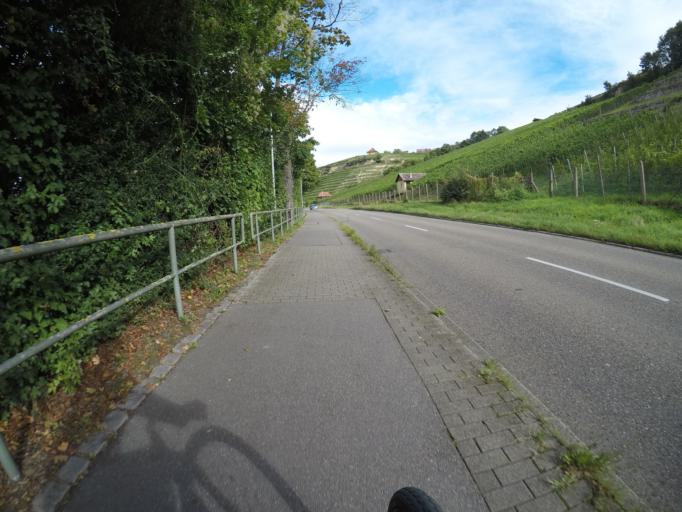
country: DE
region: Baden-Wuerttemberg
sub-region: Regierungsbezirk Stuttgart
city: Stuttgart Muehlhausen
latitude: 48.8213
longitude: 9.2281
